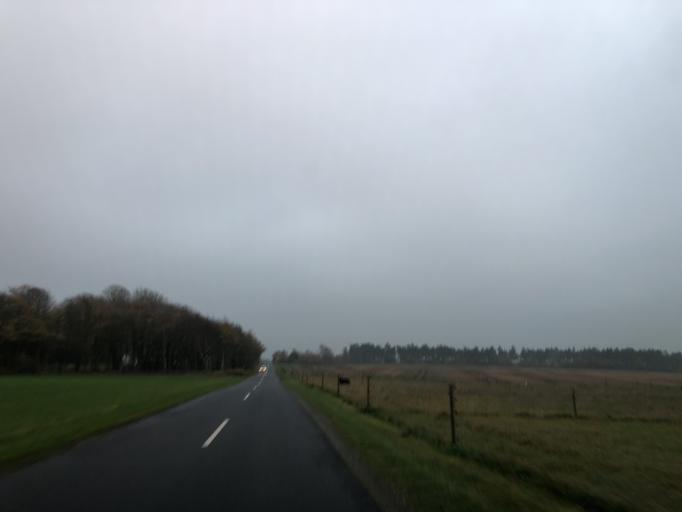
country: DK
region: Central Jutland
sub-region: Ringkobing-Skjern Kommune
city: Videbaek
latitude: 56.1900
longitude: 8.6423
